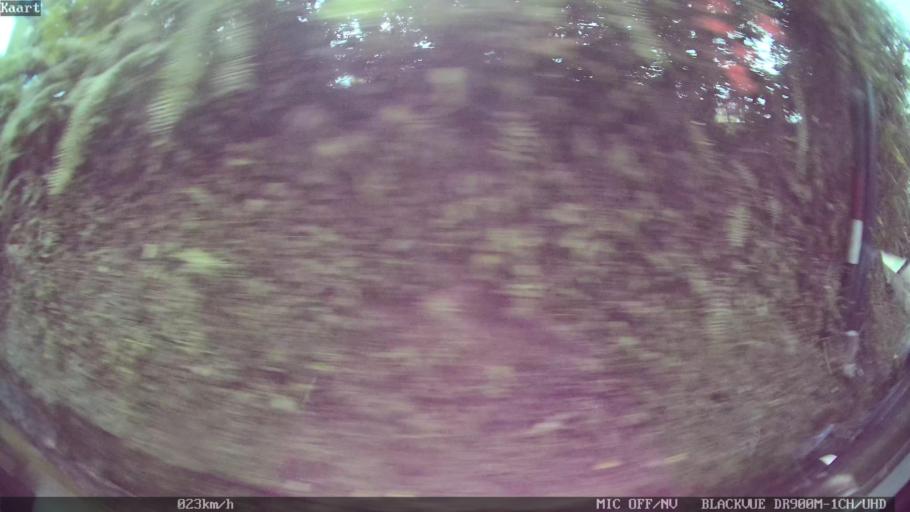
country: ID
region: Bali
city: Banjar Pesalakan
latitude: -8.5097
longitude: 115.3014
